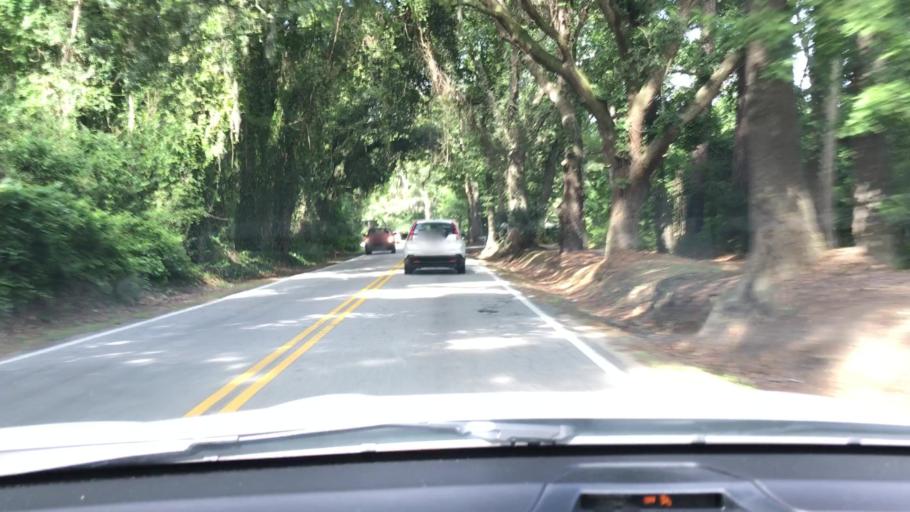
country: US
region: South Carolina
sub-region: Charleston County
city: Mount Pleasant
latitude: 32.8437
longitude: -79.8383
